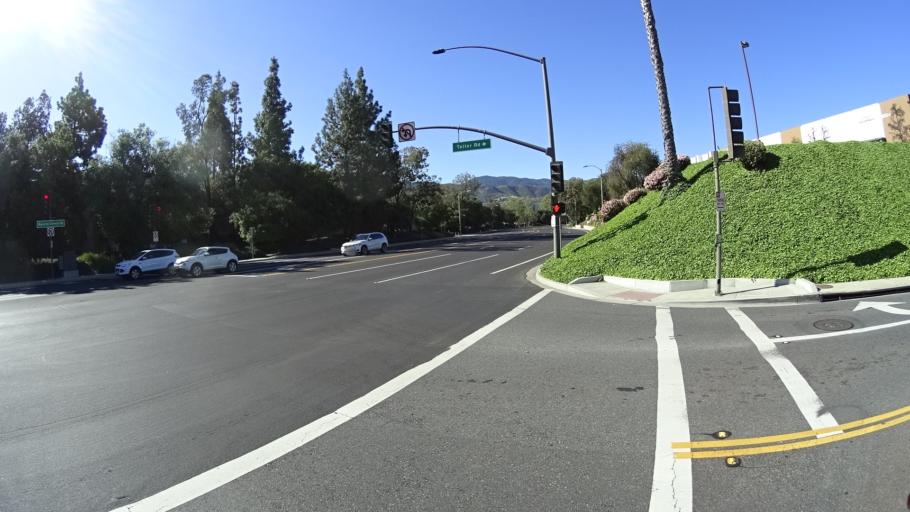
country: US
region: California
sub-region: Ventura County
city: Casa Conejo
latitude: 34.1909
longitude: -118.9242
